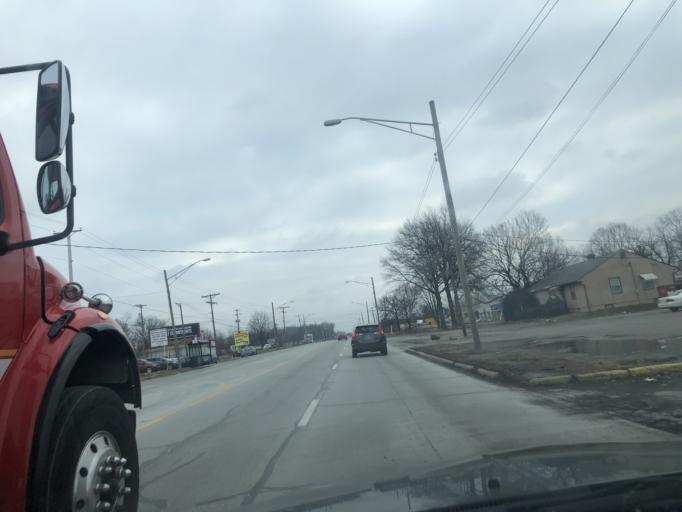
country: US
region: Ohio
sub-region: Franklin County
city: Groveport
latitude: 39.9173
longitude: -82.9140
